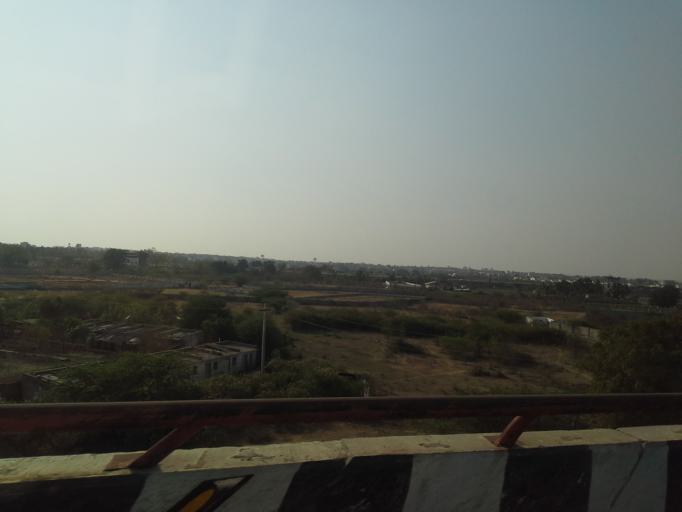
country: IN
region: Telangana
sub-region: Rangareddi
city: Sriramnagar
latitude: 17.2563
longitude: 78.3810
